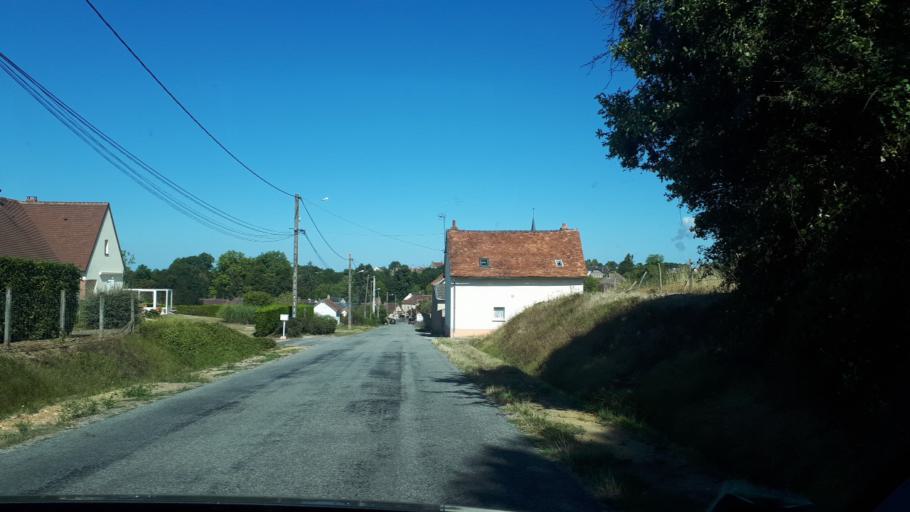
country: FR
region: Centre
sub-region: Departement du Loiret
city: Autry-le-Chatel
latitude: 47.5940
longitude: 2.6057
